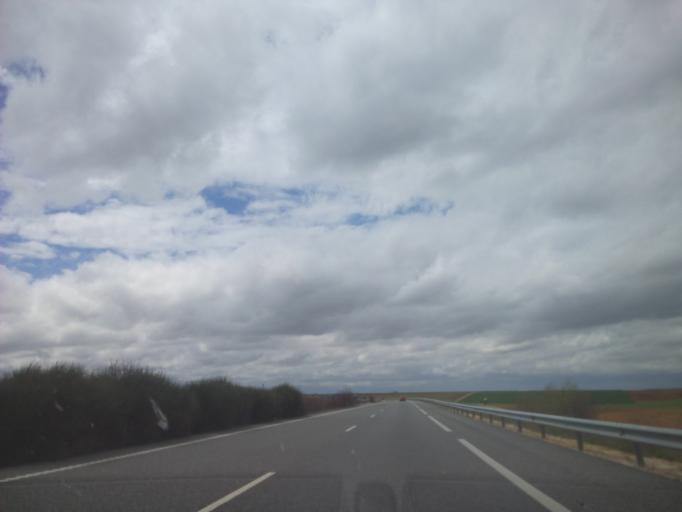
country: ES
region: Castille and Leon
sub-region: Provincia de Salamanca
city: Calvarrasa de Abajo
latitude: 40.9310
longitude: -5.5521
